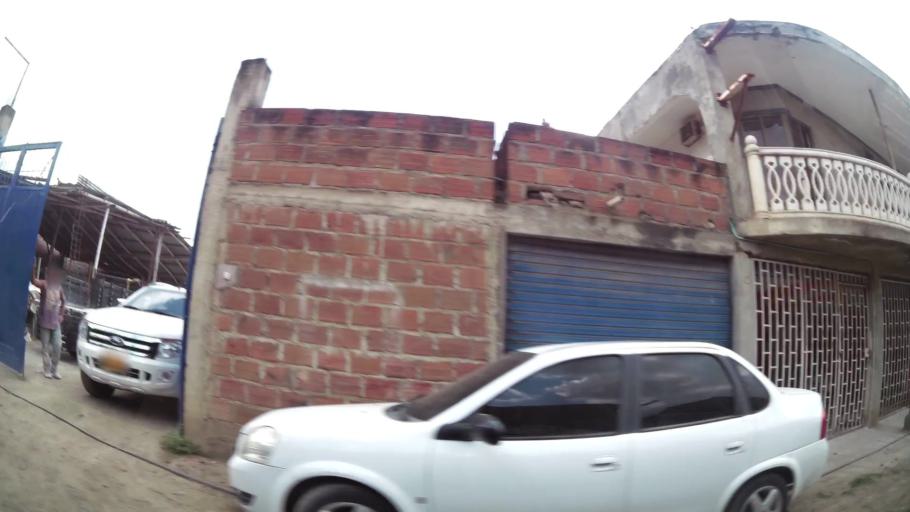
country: CO
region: Valle del Cauca
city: Cali
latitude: 3.4474
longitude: -76.4698
